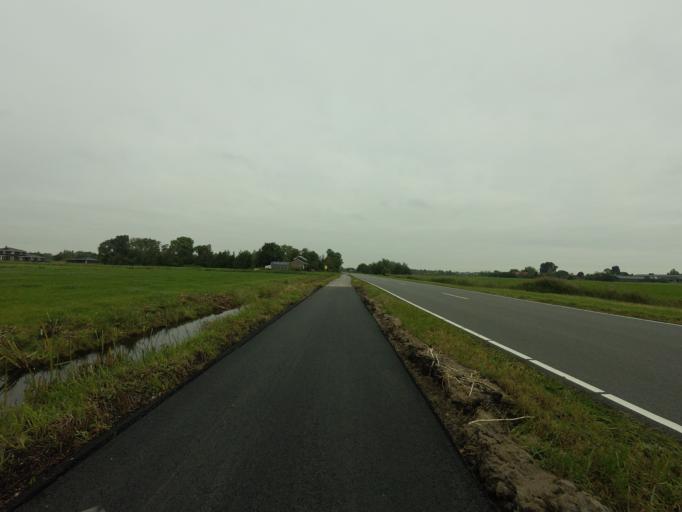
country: NL
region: Utrecht
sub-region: Gemeente De Ronde Venen
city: Mijdrecht
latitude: 52.1445
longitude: 4.8601
